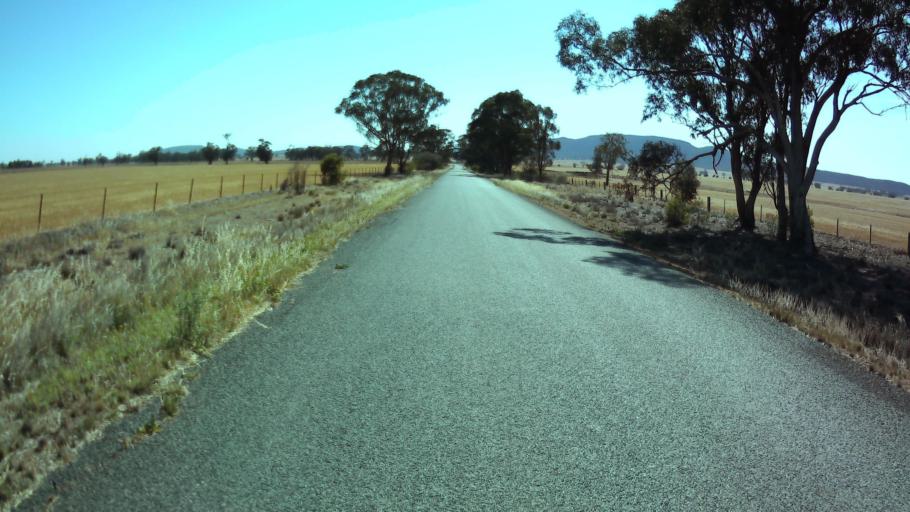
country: AU
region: New South Wales
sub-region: Weddin
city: Grenfell
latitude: -33.7507
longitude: 147.8698
